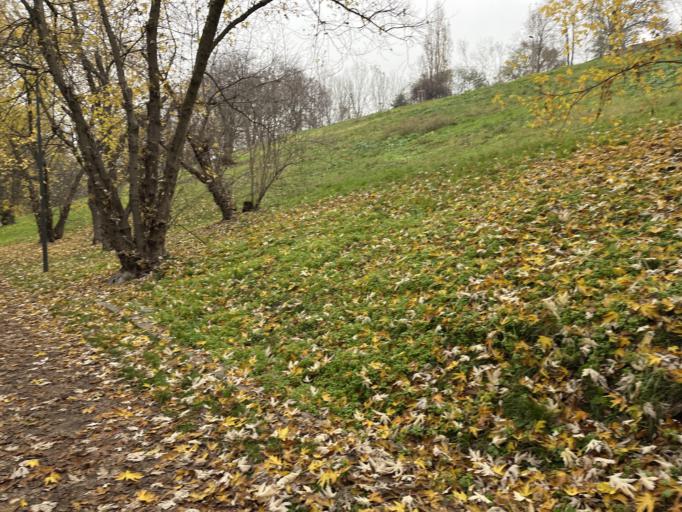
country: IT
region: Lombardy
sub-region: Citta metropolitana di Milano
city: Baranzate
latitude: 45.4903
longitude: 9.1338
